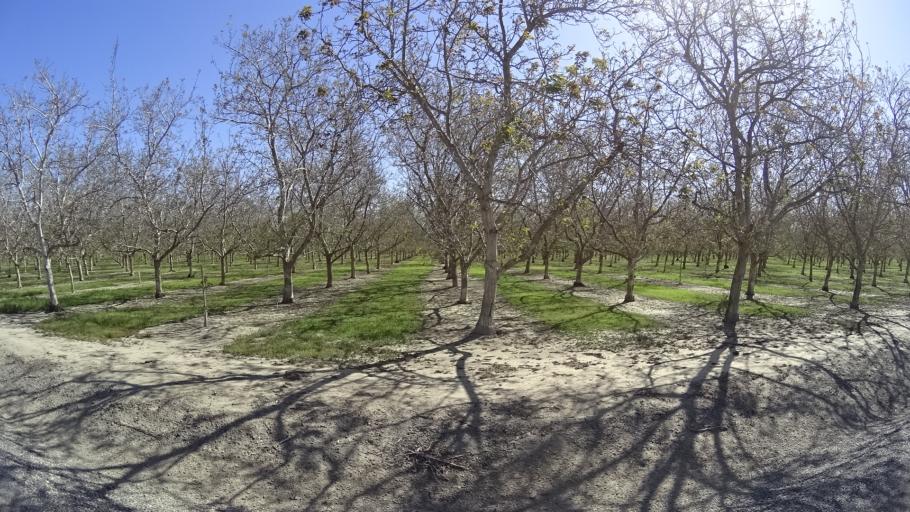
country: US
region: California
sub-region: Glenn County
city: Hamilton City
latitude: 39.7172
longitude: -122.0070
